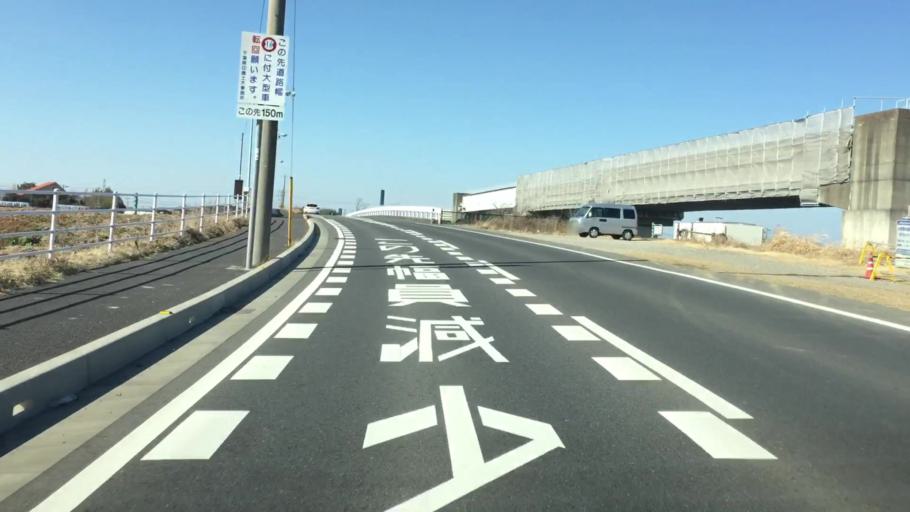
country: JP
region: Ibaraki
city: Ryugasaki
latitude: 35.8408
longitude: 140.1360
